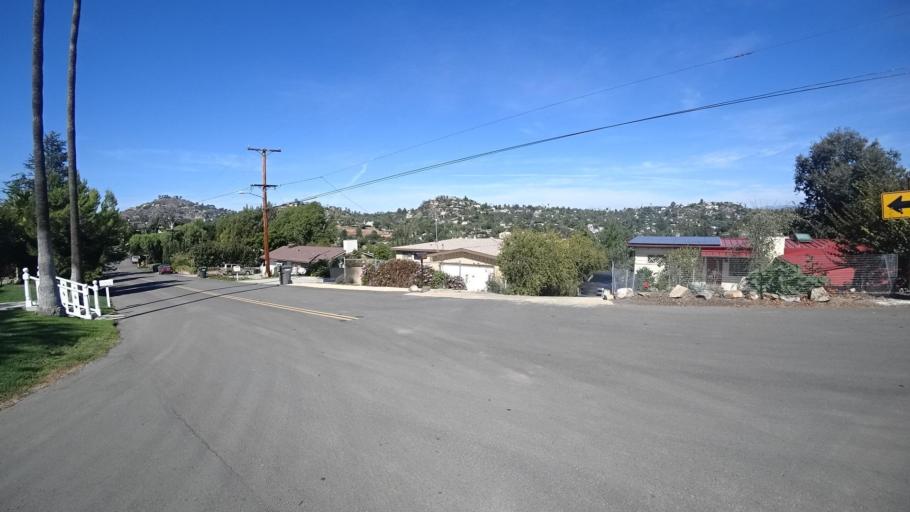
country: US
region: California
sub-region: San Diego County
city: Casa de Oro-Mount Helix
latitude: 32.7501
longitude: -116.9687
